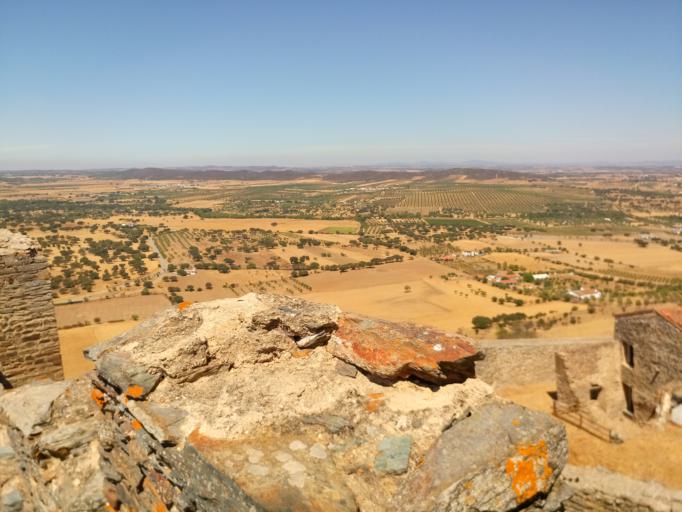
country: PT
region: Evora
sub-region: Mourao
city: Mourao
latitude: 38.4423
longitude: -7.3816
